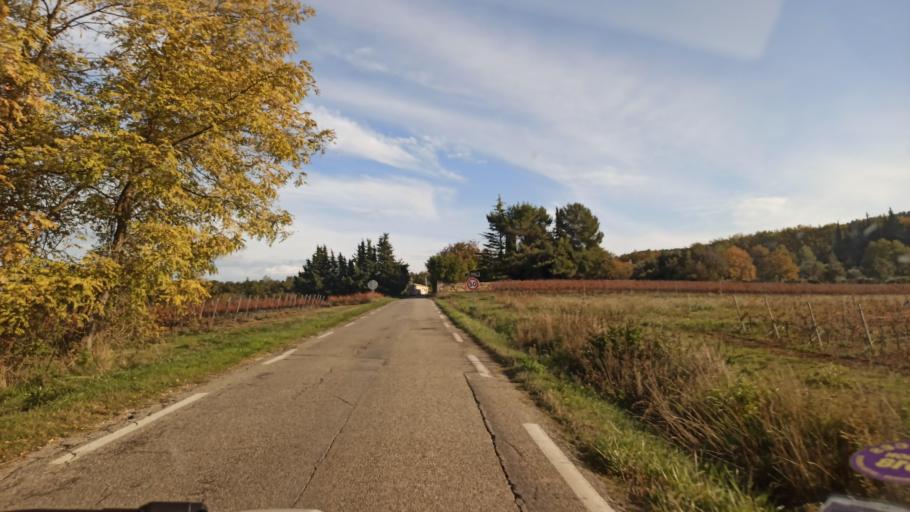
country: FR
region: Provence-Alpes-Cote d'Azur
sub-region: Departement du Vaucluse
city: Goult
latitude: 43.8429
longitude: 5.2504
